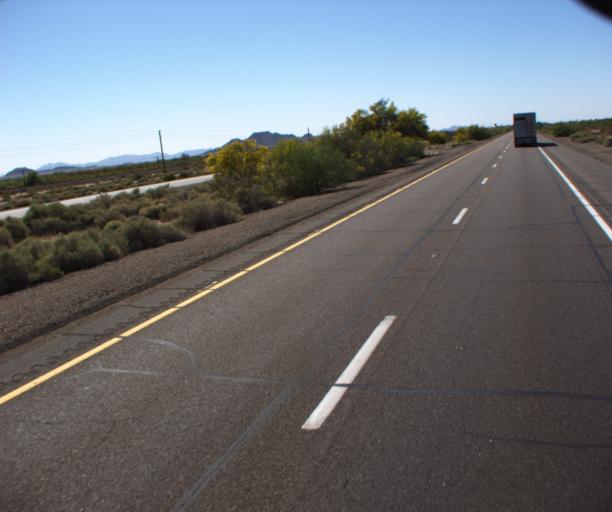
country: US
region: Arizona
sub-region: Maricopa County
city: Gila Bend
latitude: 32.8272
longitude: -113.4235
